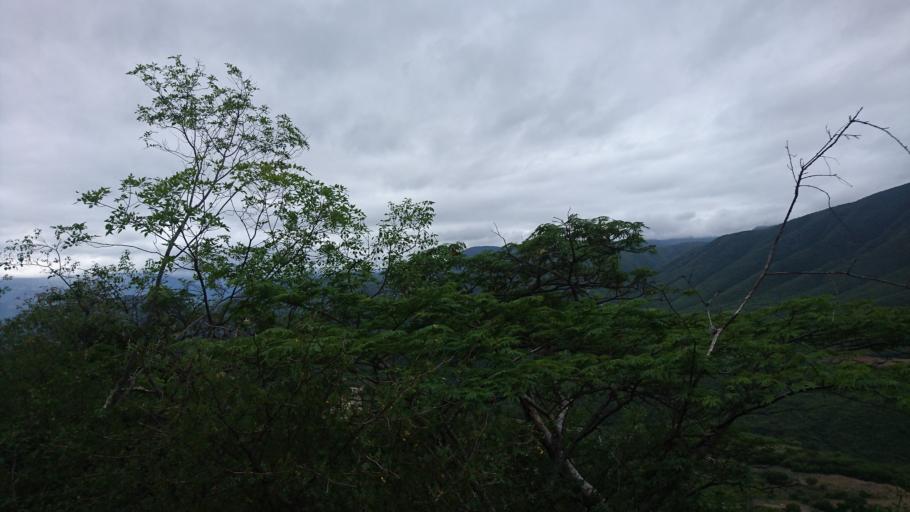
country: MX
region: Oaxaca
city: San Lorenzo Albarradas
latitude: 16.8663
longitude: -96.2741
